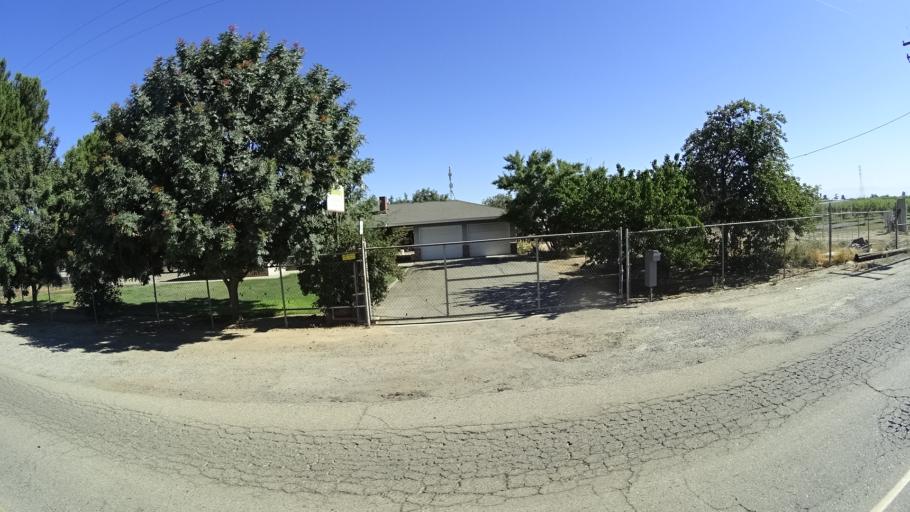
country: US
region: California
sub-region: Fresno County
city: West Park
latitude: 36.6922
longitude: -119.8250
